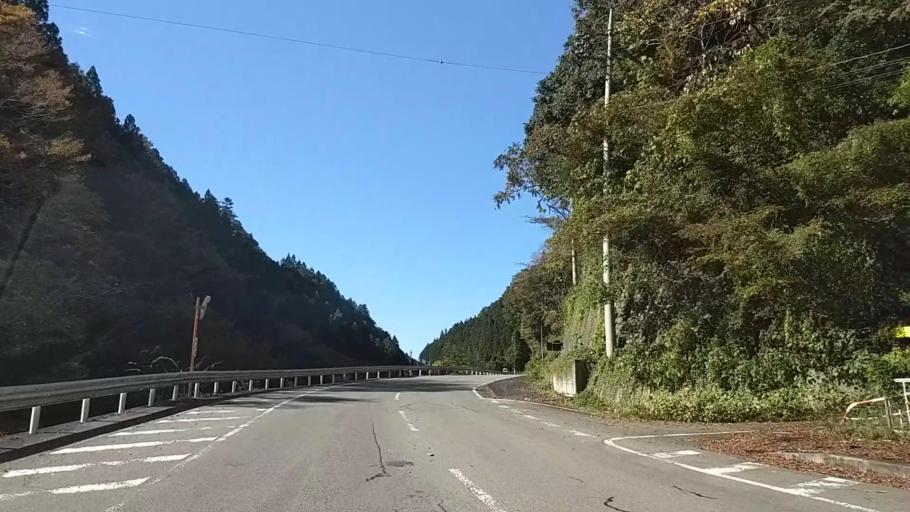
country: JP
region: Yamanashi
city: Uenohara
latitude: 35.6733
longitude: 139.0895
